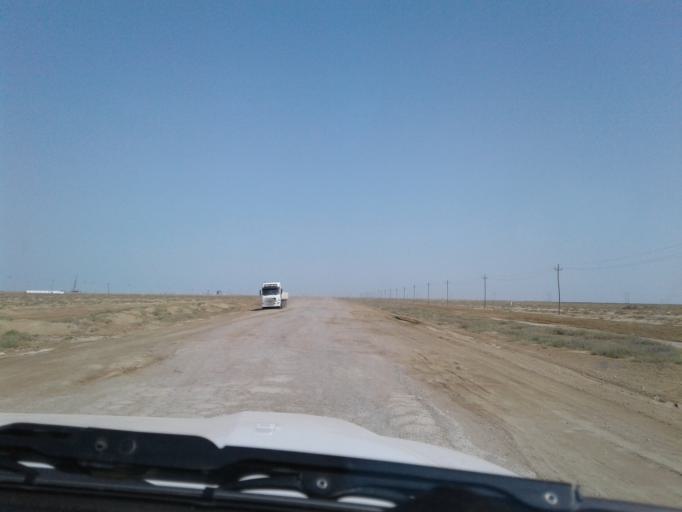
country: IR
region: Golestan
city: Gomishan
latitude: 37.7478
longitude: 53.9313
